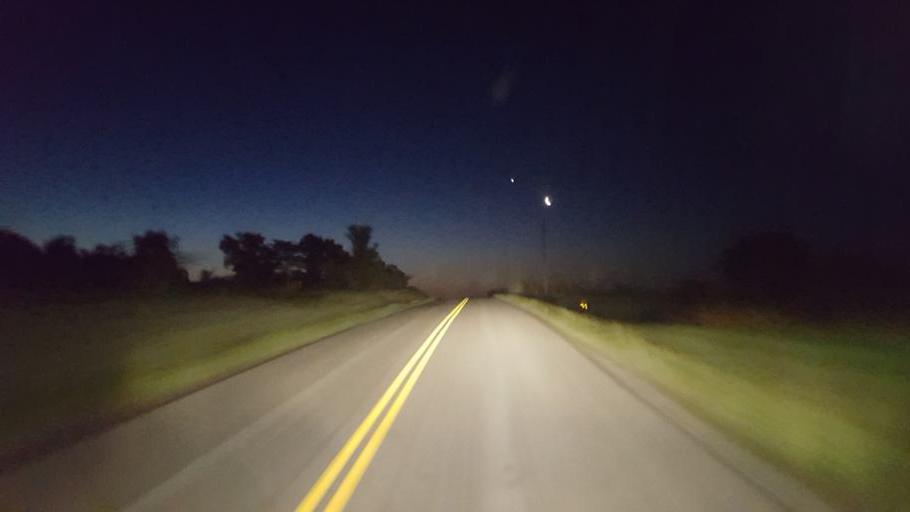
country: US
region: Iowa
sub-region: Decatur County
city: Lamoni
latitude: 40.4565
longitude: -93.8286
